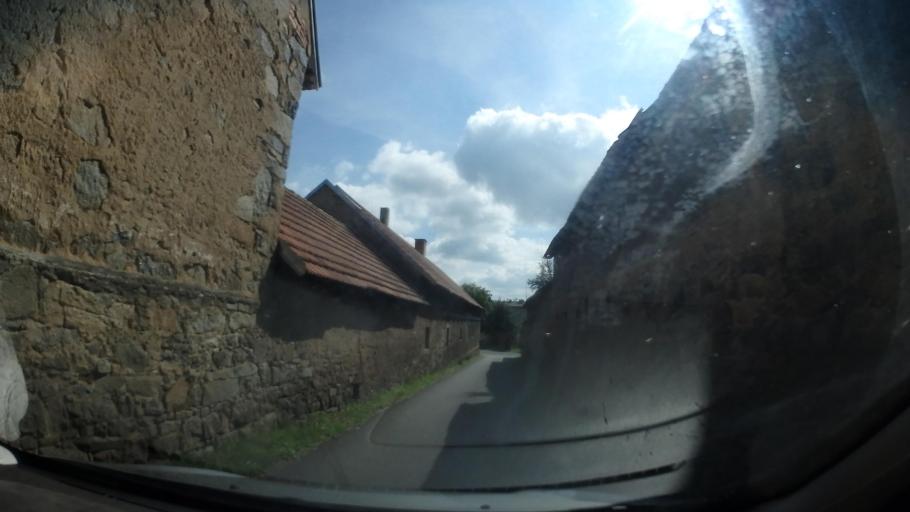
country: CZ
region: Central Bohemia
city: Krasna Hora nad Vltavou
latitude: 49.6770
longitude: 14.3192
